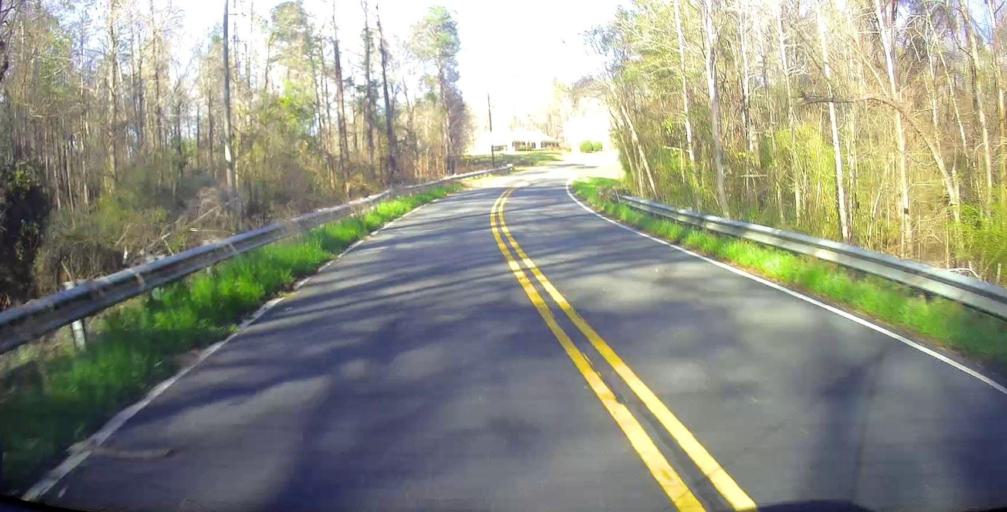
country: US
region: Georgia
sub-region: Peach County
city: Fort Valley
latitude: 32.5196
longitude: -83.9193
